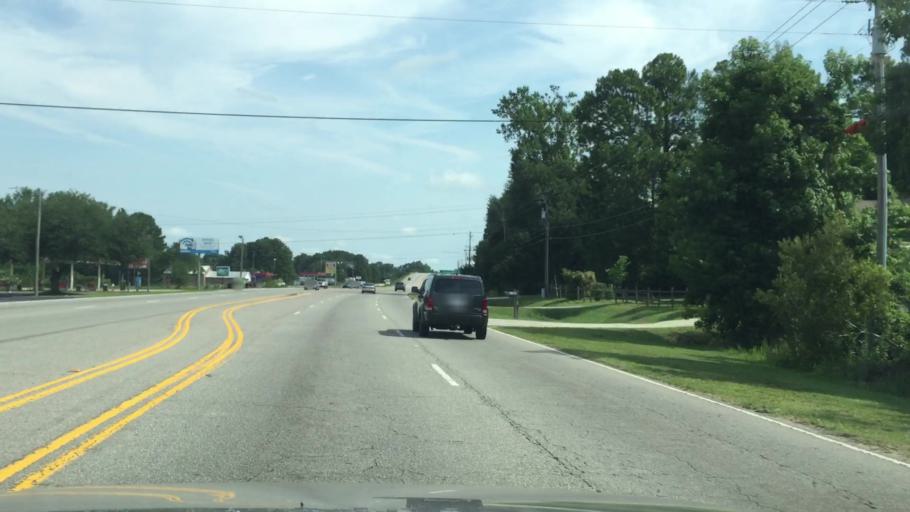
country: US
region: South Carolina
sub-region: Sumter County
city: South Sumter
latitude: 33.8994
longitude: -80.3534
